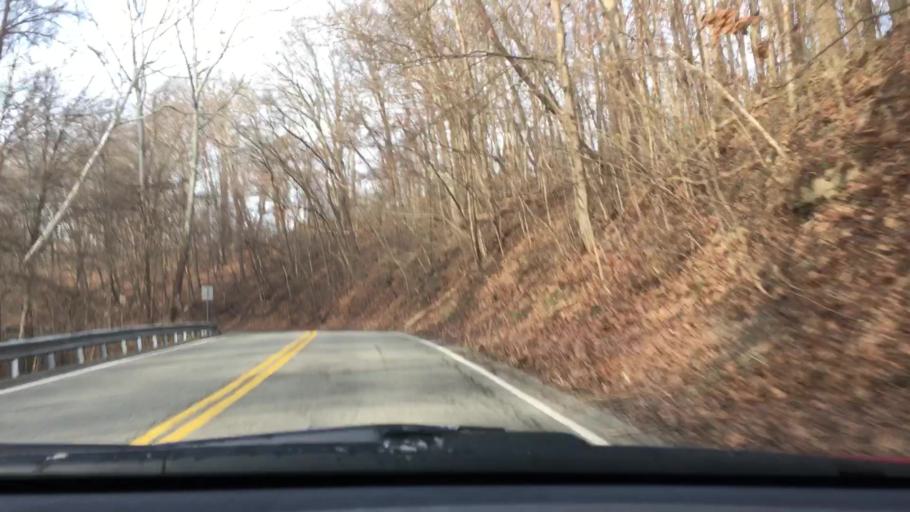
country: US
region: Pennsylvania
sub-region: Allegheny County
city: Industry
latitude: 40.2410
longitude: -79.8358
